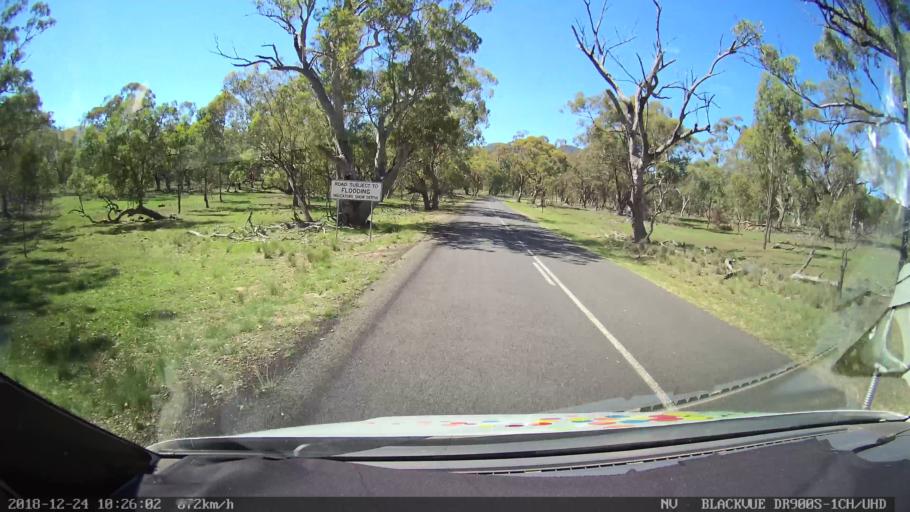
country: AU
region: New South Wales
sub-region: Liverpool Plains
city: Quirindi
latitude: -31.8053
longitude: 150.5278
